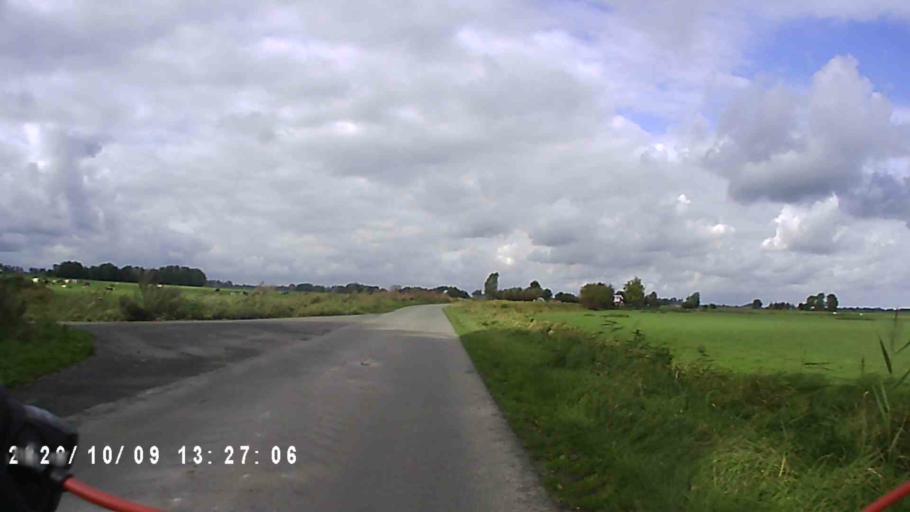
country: NL
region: Groningen
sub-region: Gemeente Zuidhorn
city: Aduard
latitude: 53.2665
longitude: 6.4619
